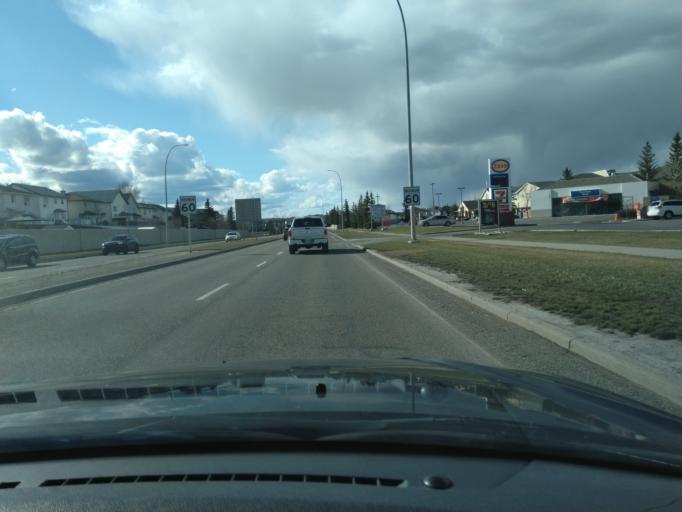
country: CA
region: Alberta
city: Calgary
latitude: 51.1416
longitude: -114.1828
